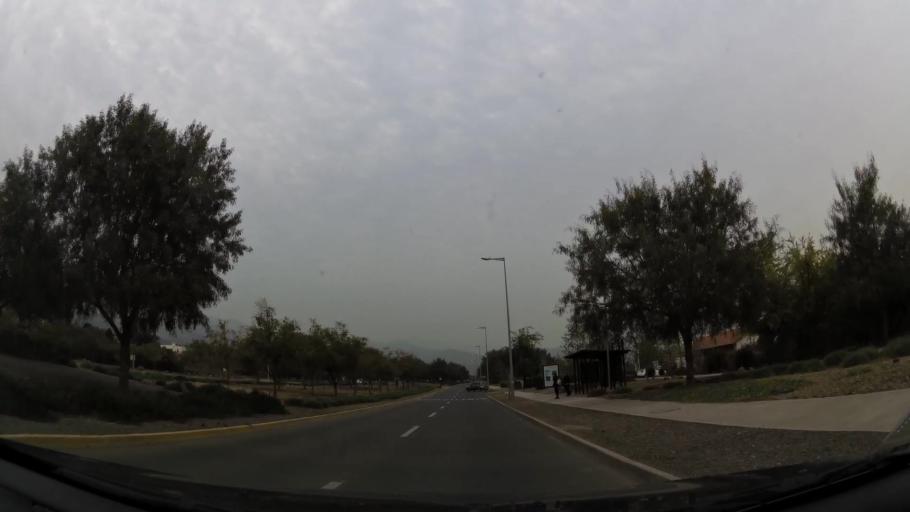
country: CL
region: Santiago Metropolitan
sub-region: Provincia de Chacabuco
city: Chicureo Abajo
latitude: -33.2596
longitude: -70.6269
